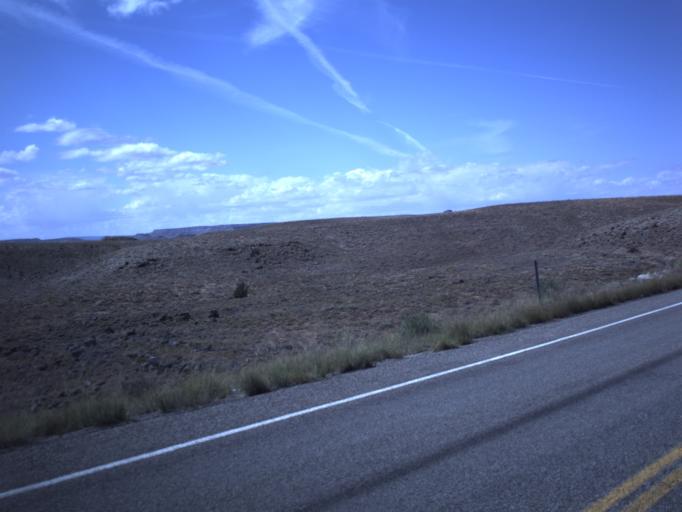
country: US
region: Colorado
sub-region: Montezuma County
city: Towaoc
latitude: 37.1754
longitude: -109.1080
